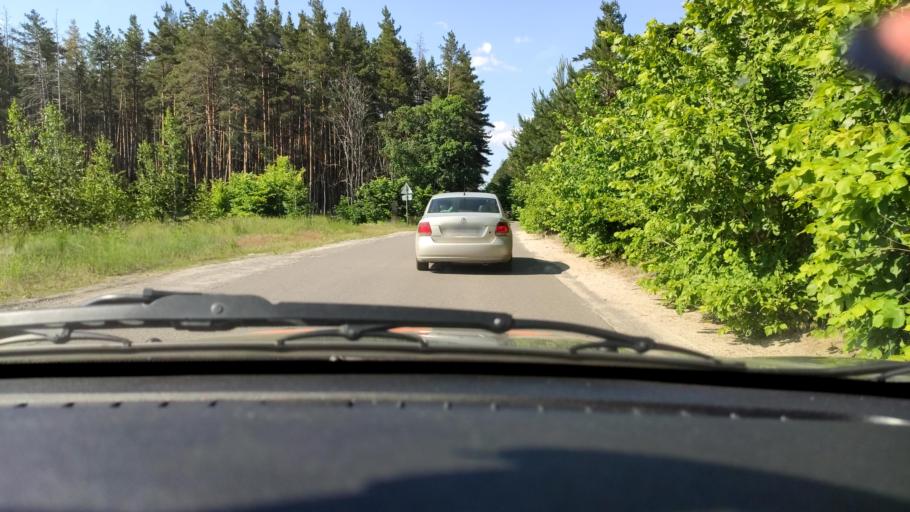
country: RU
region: Voronezj
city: Somovo
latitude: 51.7608
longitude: 39.3656
